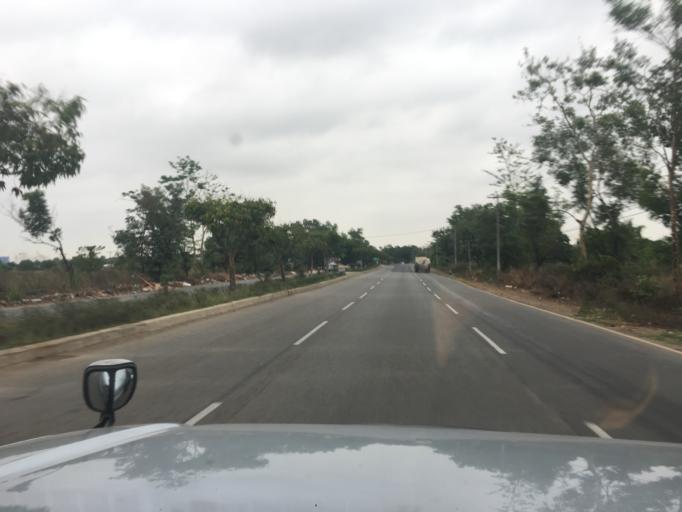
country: MM
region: Bago
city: Bago
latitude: 17.2307
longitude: 96.4579
